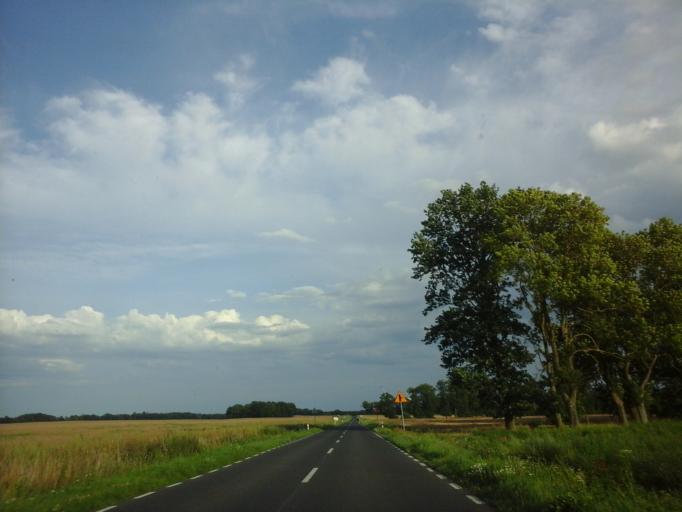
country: PL
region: West Pomeranian Voivodeship
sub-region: Powiat kamienski
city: Kamien Pomorski
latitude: 53.8998
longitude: 14.8604
